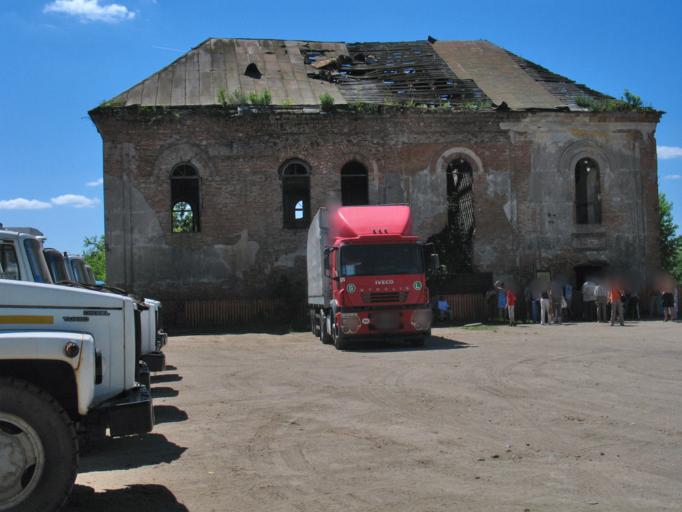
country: BY
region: Brest
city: Ruzhany
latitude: 52.8655
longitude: 24.8886
